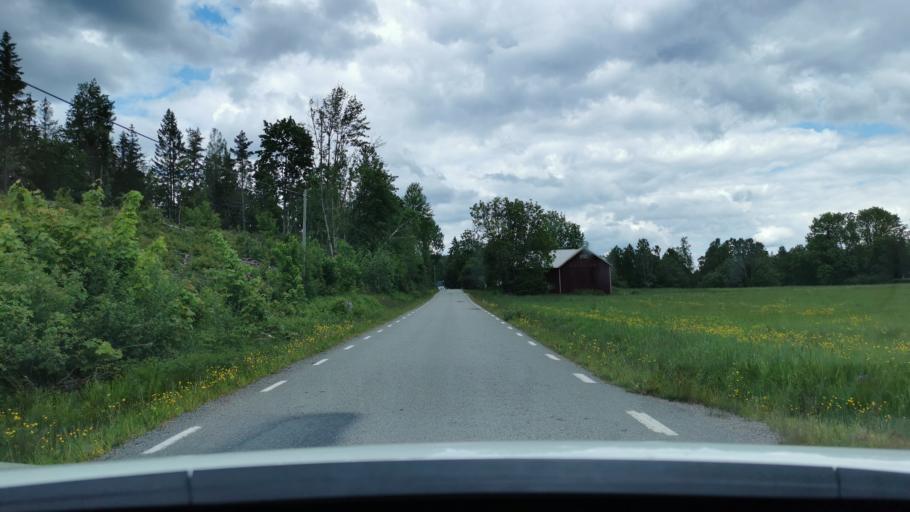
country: SE
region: Vaestra Goetaland
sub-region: Bengtsfors Kommun
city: Dals Langed
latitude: 58.7978
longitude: 12.3286
